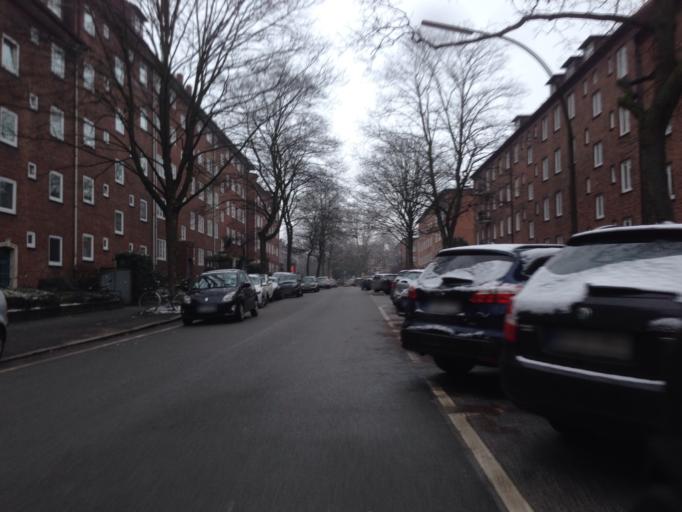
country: DE
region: Hamburg
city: Marienthal
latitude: 53.5801
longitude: 10.0639
